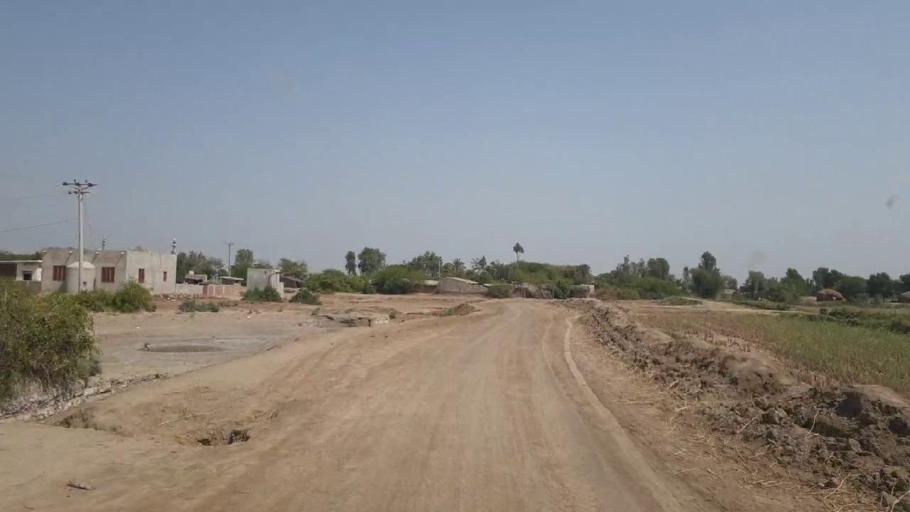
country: PK
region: Sindh
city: Jati
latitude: 24.4863
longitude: 68.5574
